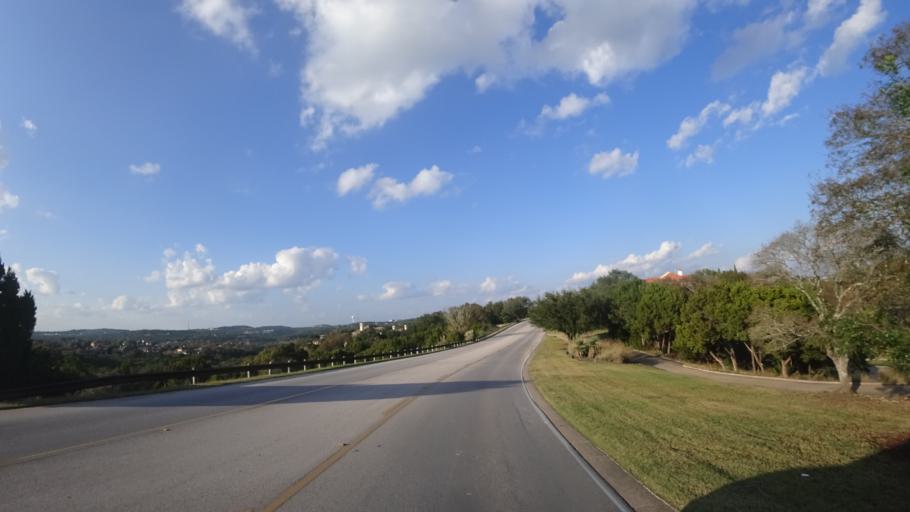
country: US
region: Texas
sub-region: Travis County
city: Barton Creek
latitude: 30.2930
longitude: -97.8625
